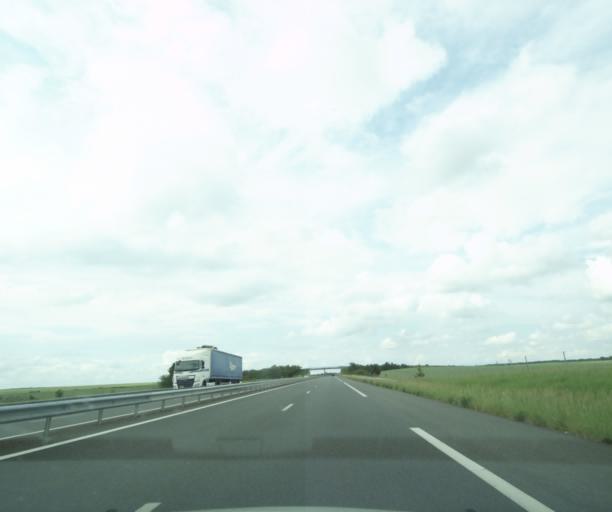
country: FR
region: Centre
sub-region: Departement du Cher
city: Chateauneuf-sur-Cher
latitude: 46.8227
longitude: 2.4129
